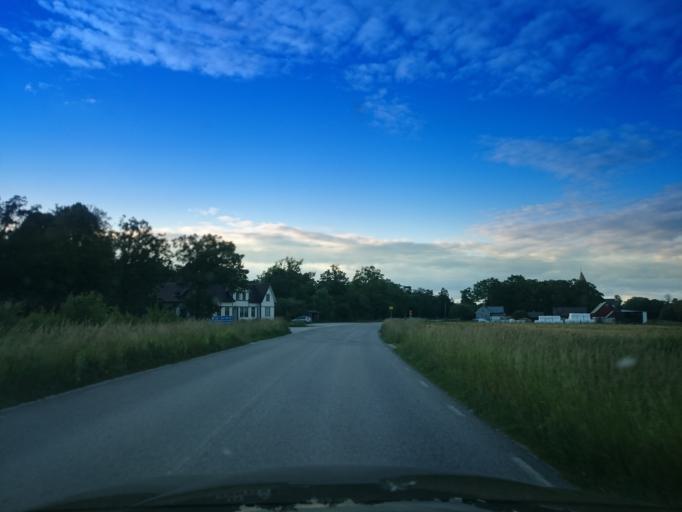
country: SE
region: Gotland
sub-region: Gotland
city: Hemse
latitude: 57.3085
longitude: 18.3799
